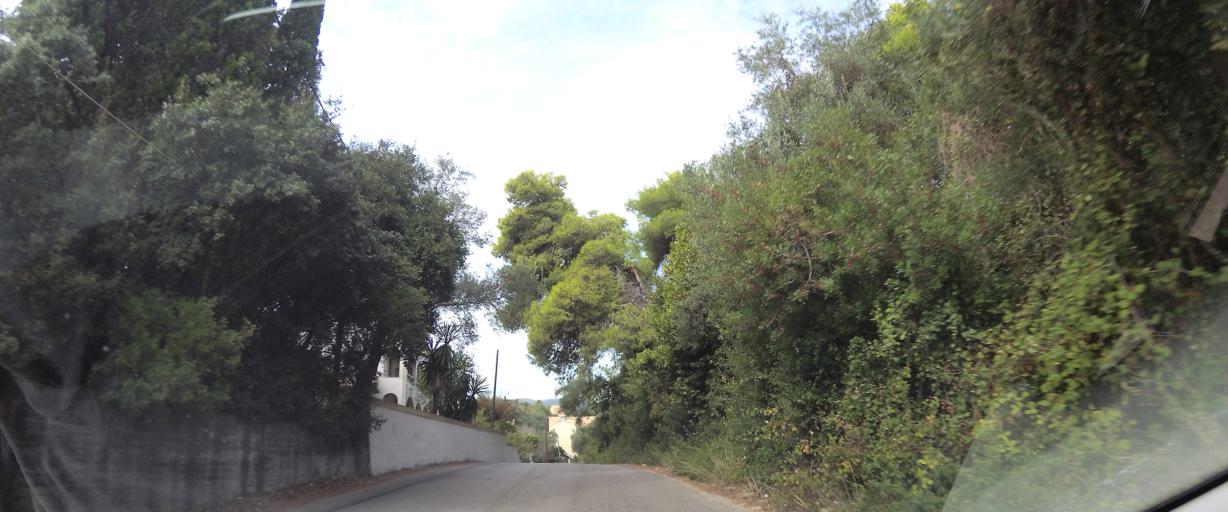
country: GR
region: Ionian Islands
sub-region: Nomos Kerkyras
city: Kontokali
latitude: 39.6871
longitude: 19.8323
